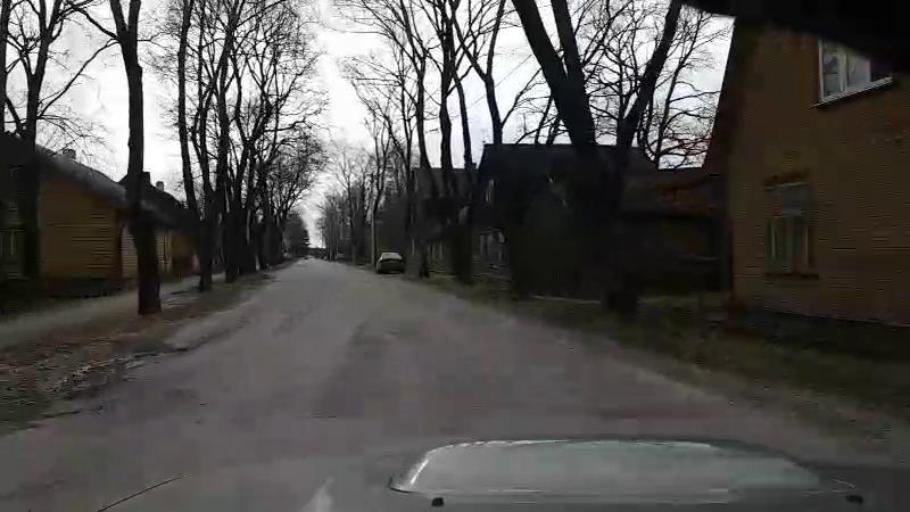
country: EE
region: Jaervamaa
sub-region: Paide linn
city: Paide
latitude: 58.8897
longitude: 25.5636
